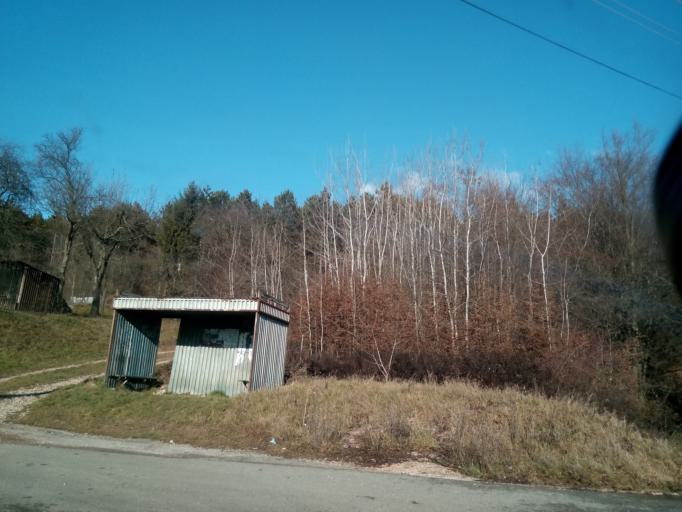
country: SK
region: Kosicky
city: Roznava
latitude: 48.6600
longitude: 20.4852
